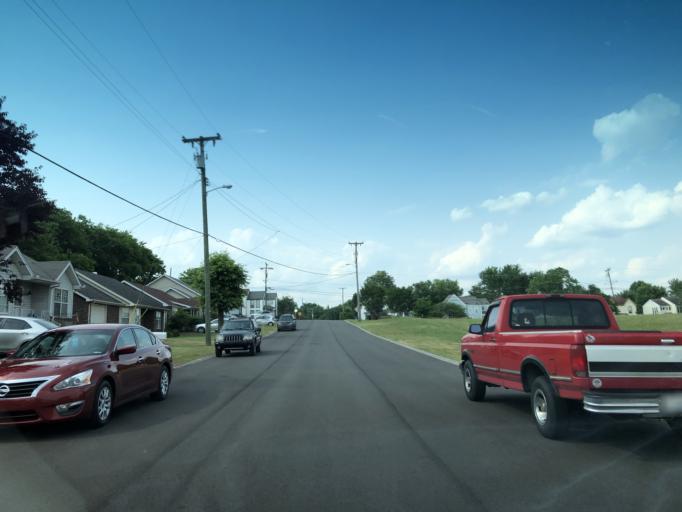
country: US
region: Tennessee
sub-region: Davidson County
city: Goodlettsville
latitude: 36.2722
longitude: -86.7167
